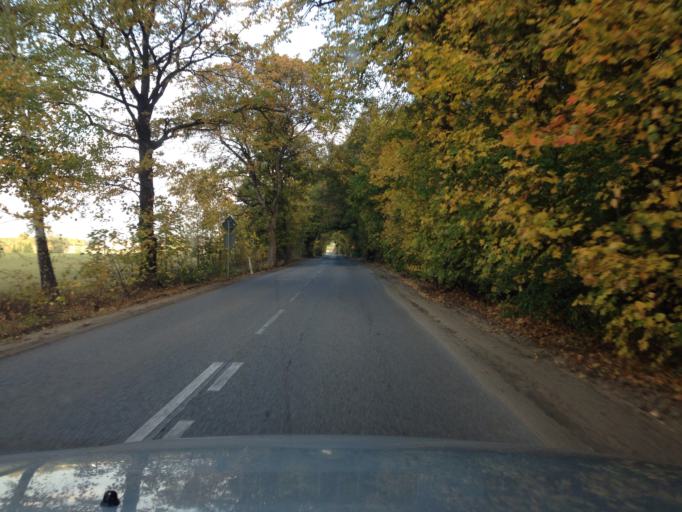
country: PL
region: Pomeranian Voivodeship
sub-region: Powiat starogardzki
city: Lubichowo
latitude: 53.8107
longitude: 18.4542
